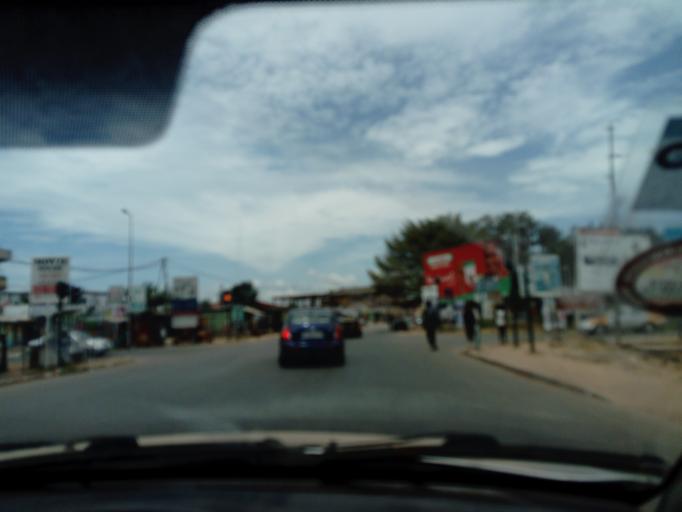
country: GH
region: Central
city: Cape Coast
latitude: 5.1280
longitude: -1.2737
